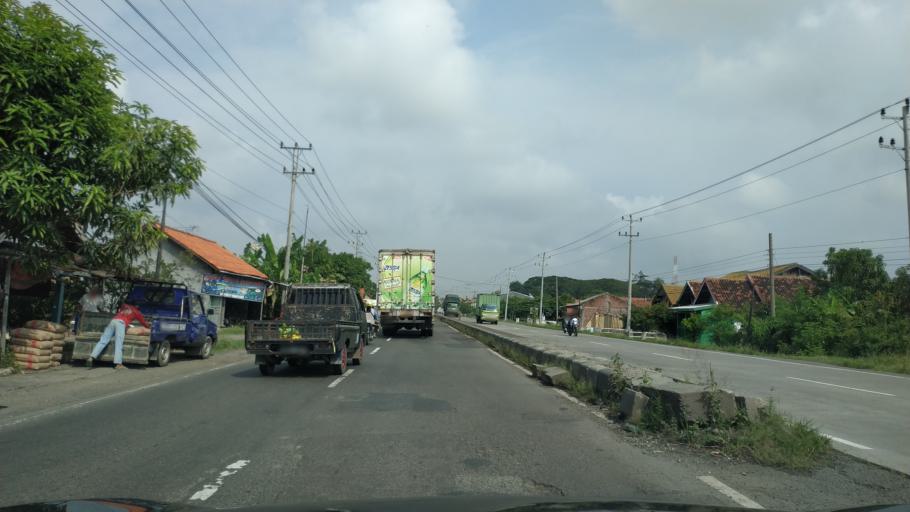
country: ID
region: Central Java
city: Bulakamba
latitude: -6.8745
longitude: 108.9360
